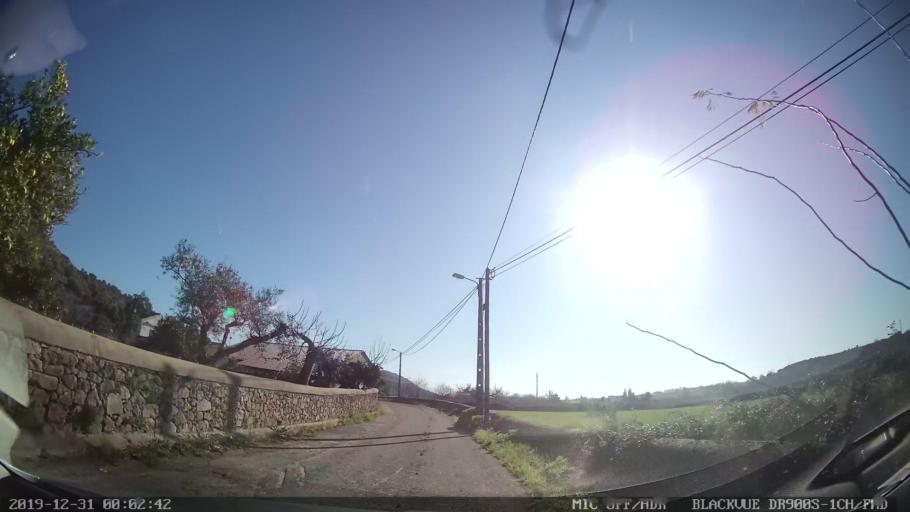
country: PT
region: Castelo Branco
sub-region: Idanha-A-Nova
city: Idanha-a-Nova
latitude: 39.9164
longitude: -7.2221
